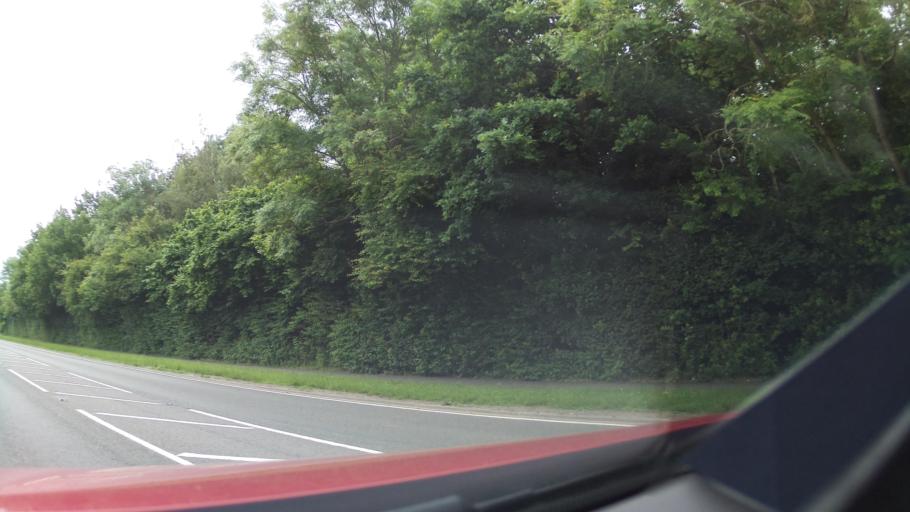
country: GB
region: England
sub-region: Leicestershire
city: Coalville
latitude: 52.7280
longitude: -1.3612
